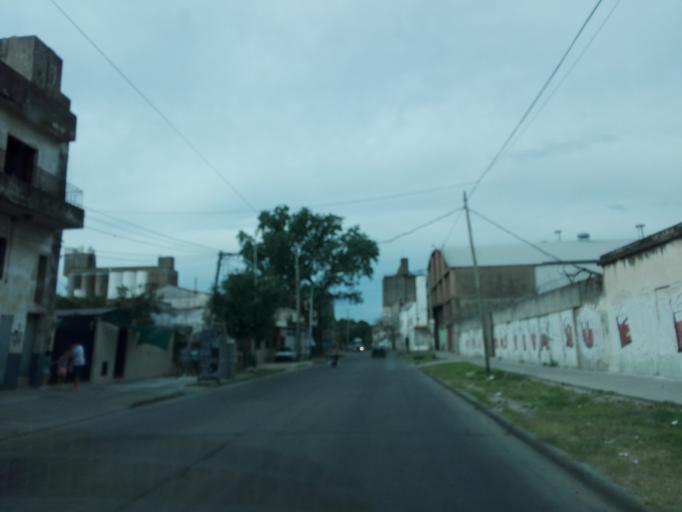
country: AR
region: Buenos Aires
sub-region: Partido de Lanus
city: Lanus
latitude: -34.6992
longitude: -58.3624
